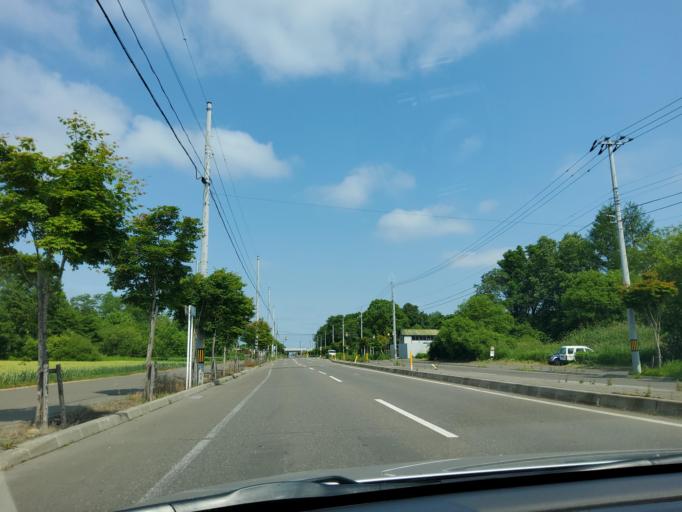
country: JP
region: Hokkaido
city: Obihiro
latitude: 42.9147
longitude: 143.1021
